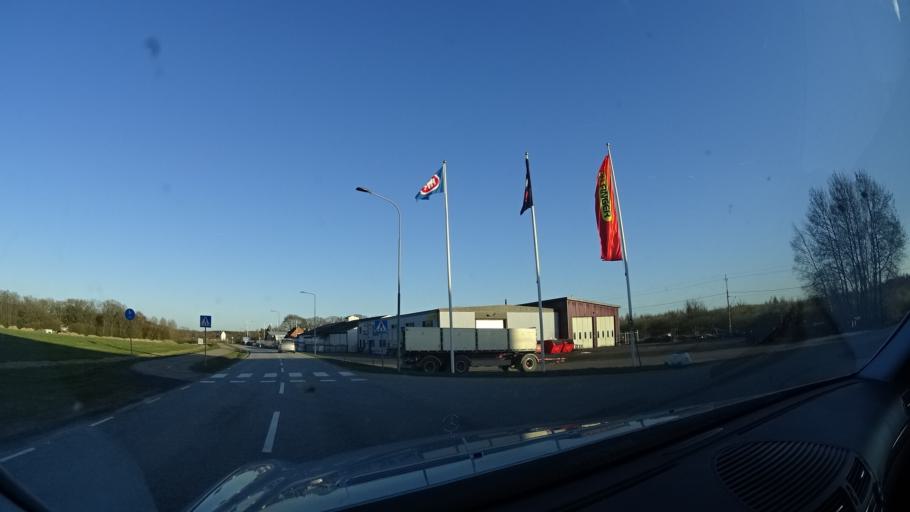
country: SE
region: Skane
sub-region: Svalovs Kommun
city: Kagerod
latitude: 56.0043
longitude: 13.0806
